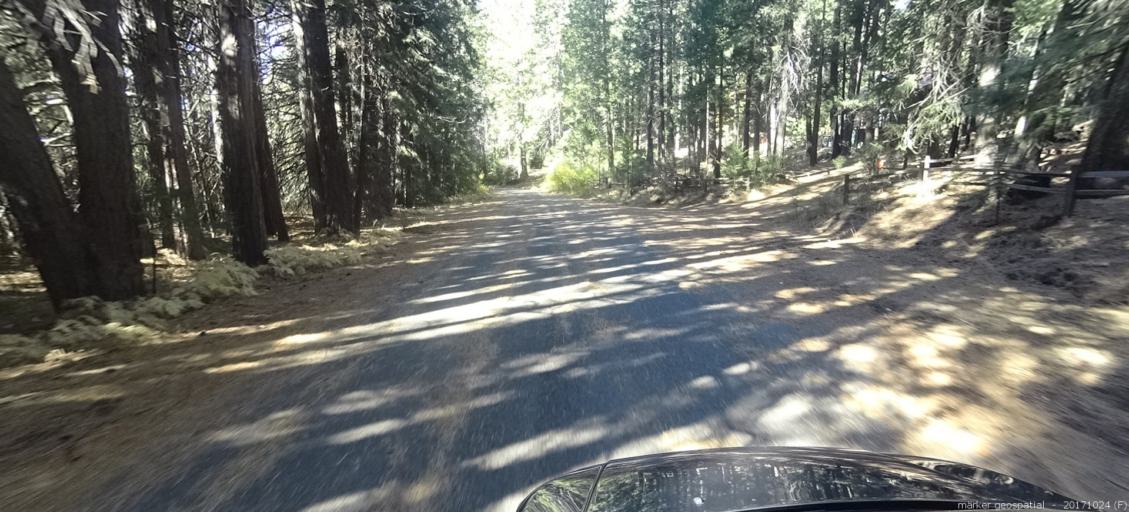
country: US
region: California
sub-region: Shasta County
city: Shingletown
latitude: 40.5177
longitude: -121.6777
